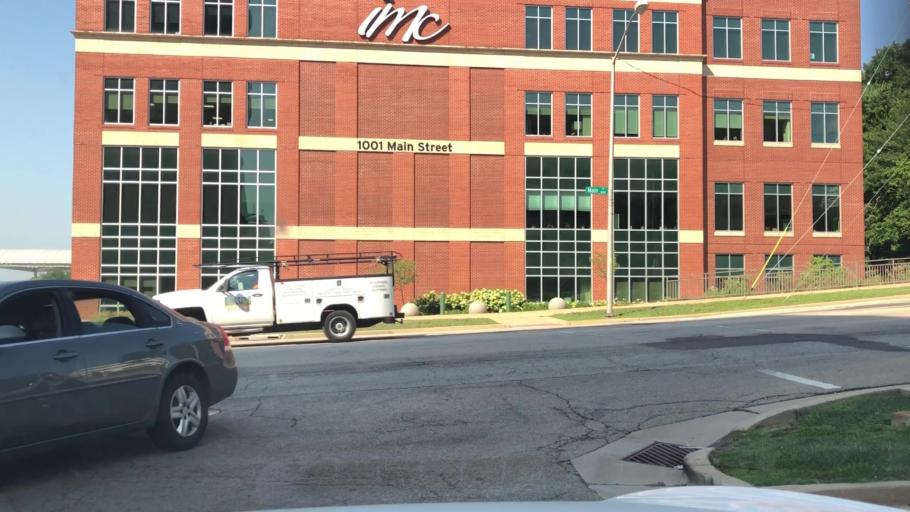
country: US
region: Illinois
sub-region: Peoria County
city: Peoria
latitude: 40.6988
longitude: -89.5967
